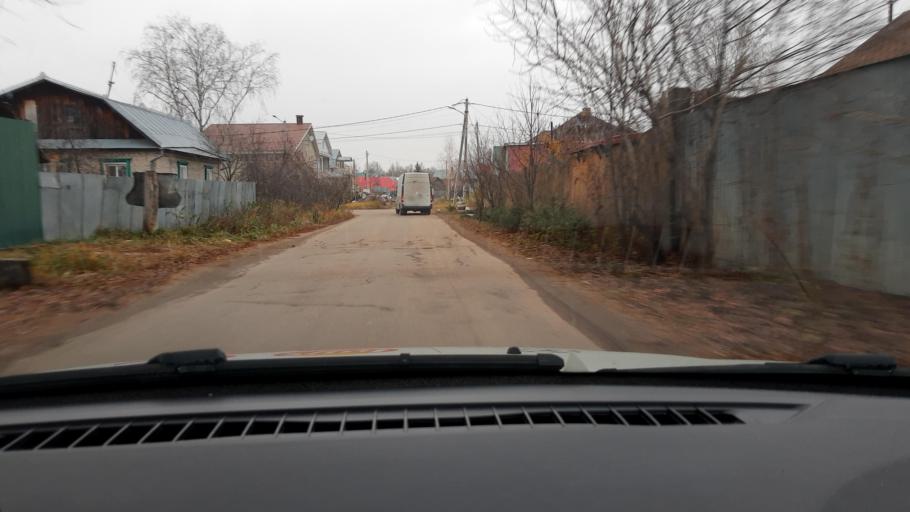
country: RU
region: Nizjnij Novgorod
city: Burevestnik
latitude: 56.2026
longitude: 43.7777
